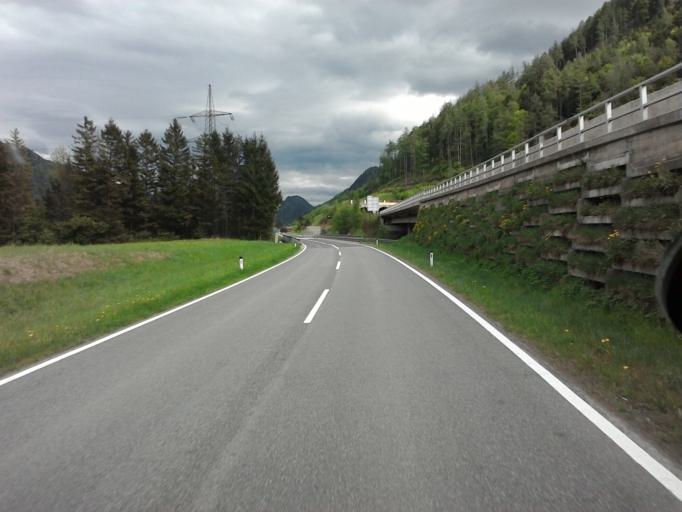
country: AT
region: Upper Austria
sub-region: Politischer Bezirk Kirchdorf an der Krems
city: Rossleithen
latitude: 47.7683
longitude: 14.1861
